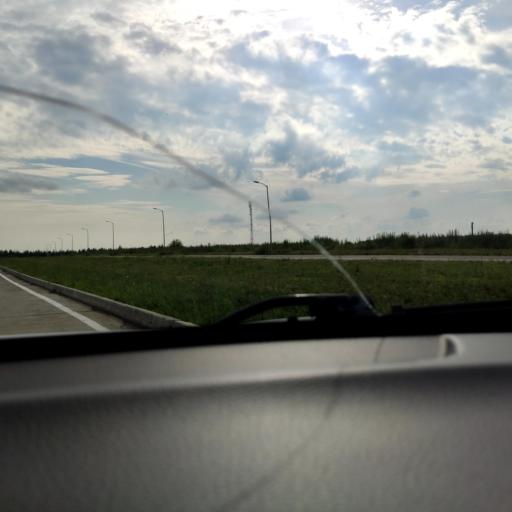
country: RU
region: Tatarstan
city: Sviyazhsk
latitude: 55.7455
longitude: 48.7365
